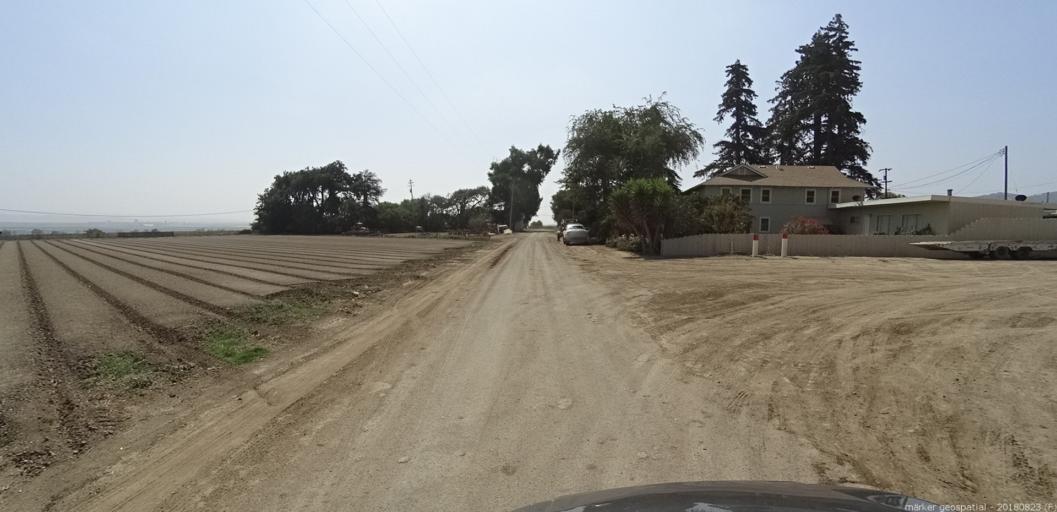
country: US
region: California
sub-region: Monterey County
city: King City
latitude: 36.2331
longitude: -121.1764
